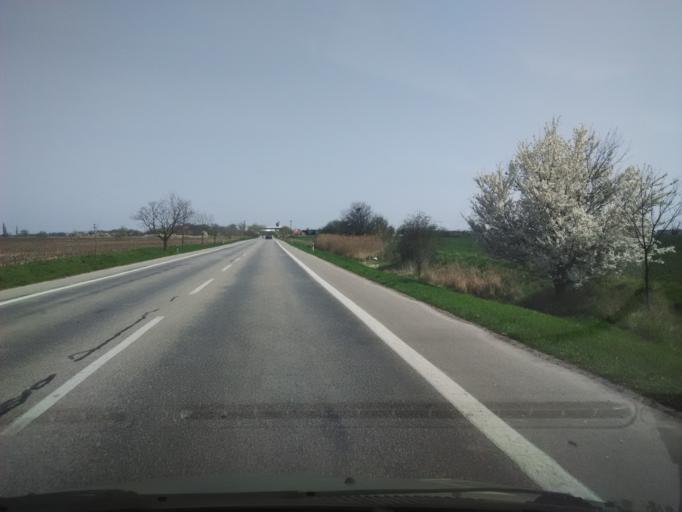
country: SK
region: Nitriansky
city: Sellye
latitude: 48.1366
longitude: 18.0119
